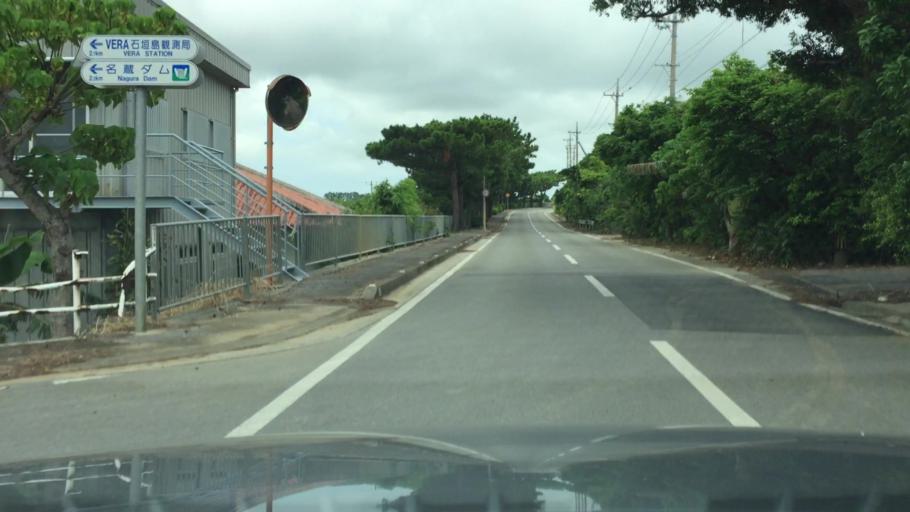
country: JP
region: Okinawa
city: Ishigaki
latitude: 24.3938
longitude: 124.1685
